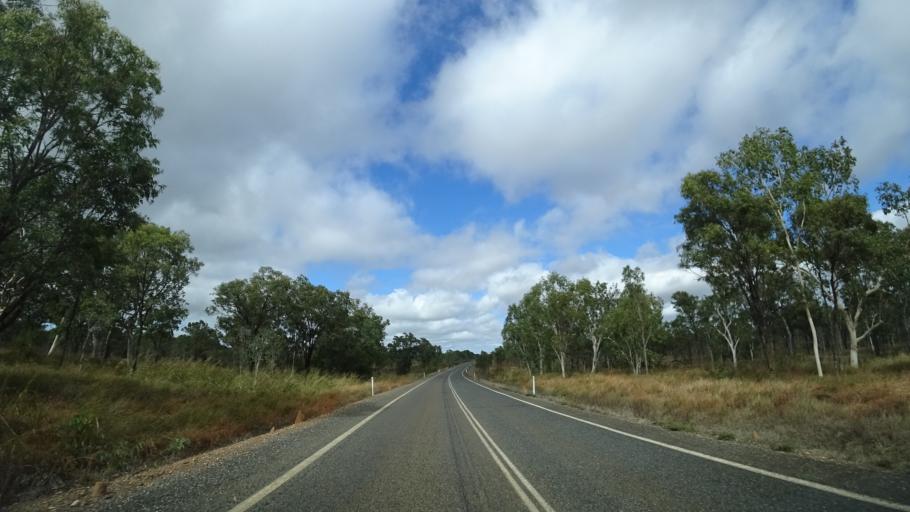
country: AU
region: Queensland
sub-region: Cook
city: Cooktown
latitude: -15.8754
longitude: 144.8608
